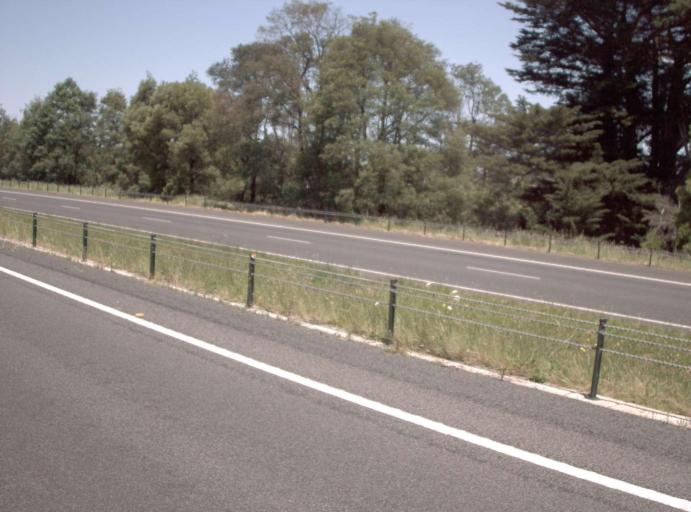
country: AU
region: Victoria
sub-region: Baw Baw
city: Warragul
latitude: -38.1648
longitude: 145.9137
